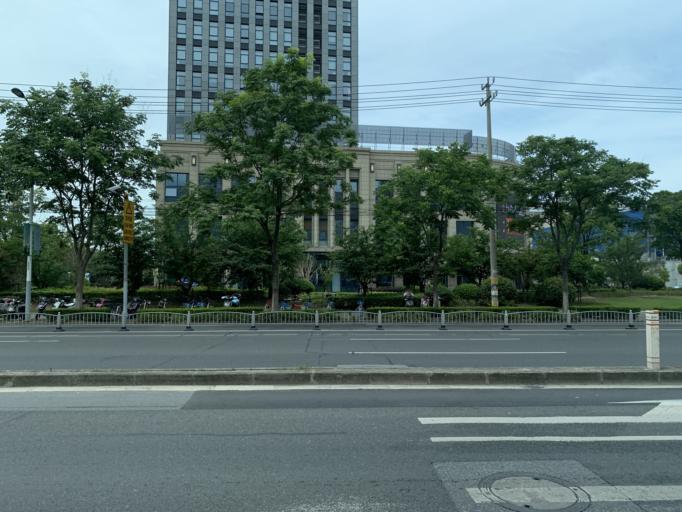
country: CN
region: Shanghai Shi
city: Kangqiao
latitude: 31.1606
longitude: 121.5598
